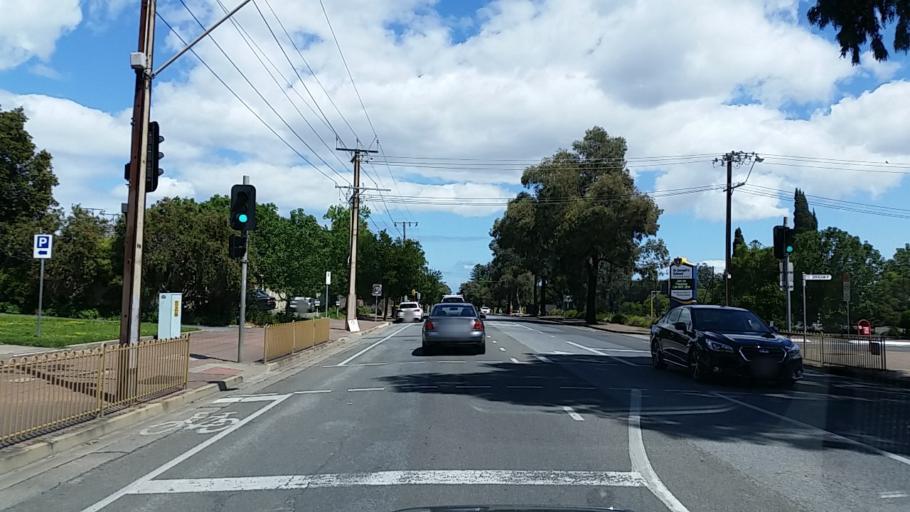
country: AU
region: South Australia
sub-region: Burnside
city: Kensington Gardens
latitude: -34.9135
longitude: 138.6669
